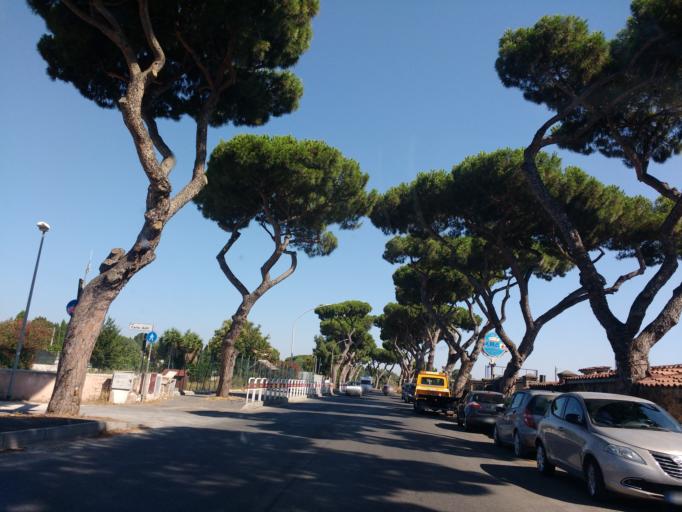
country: IT
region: Latium
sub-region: Citta metropolitana di Roma Capitale
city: Acilia-Castel Fusano-Ostia Antica
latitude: 41.7546
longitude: 12.3075
